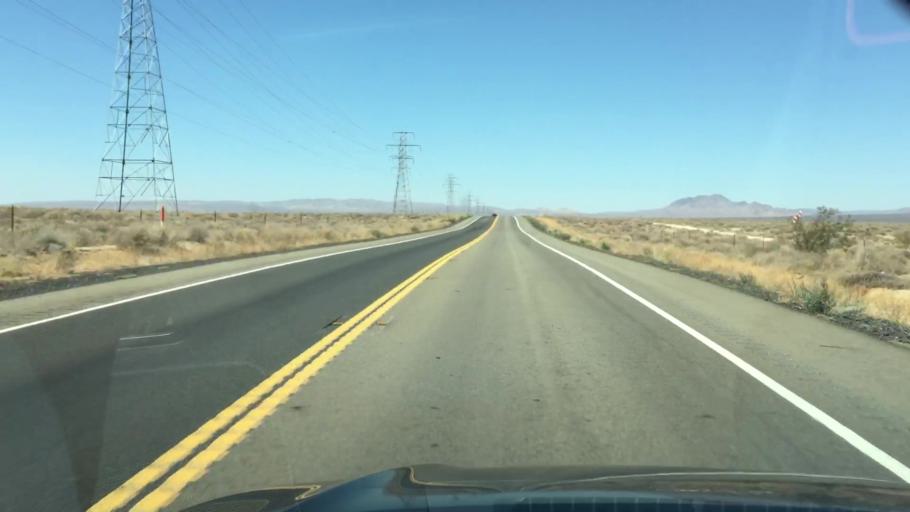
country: US
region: California
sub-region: Kern County
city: Boron
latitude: 35.1339
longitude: -117.5810
